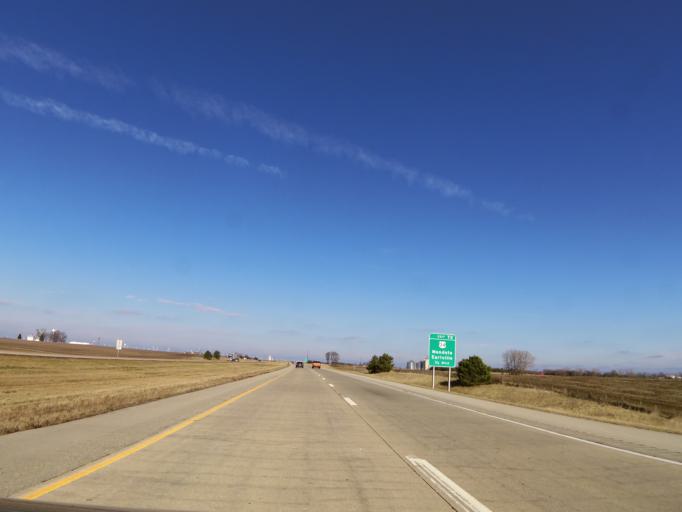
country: US
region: Illinois
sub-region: LaSalle County
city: Mendota
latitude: 41.5424
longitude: -89.0597
